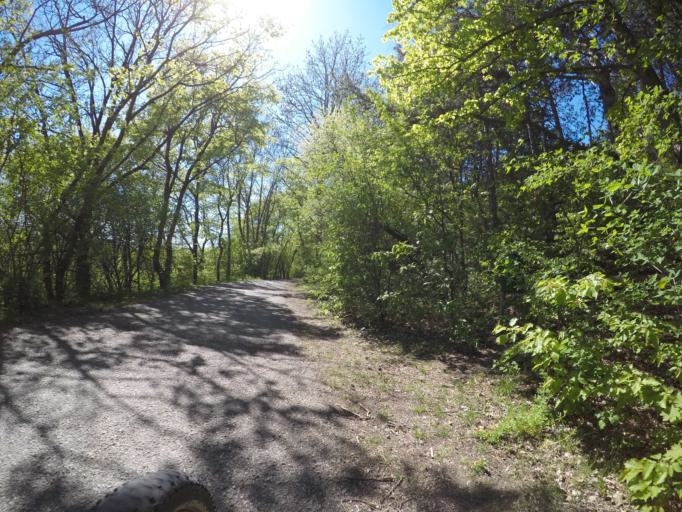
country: AT
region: Lower Austria
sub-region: Politischer Bezirk Modling
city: Modling
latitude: 48.0770
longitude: 16.2805
